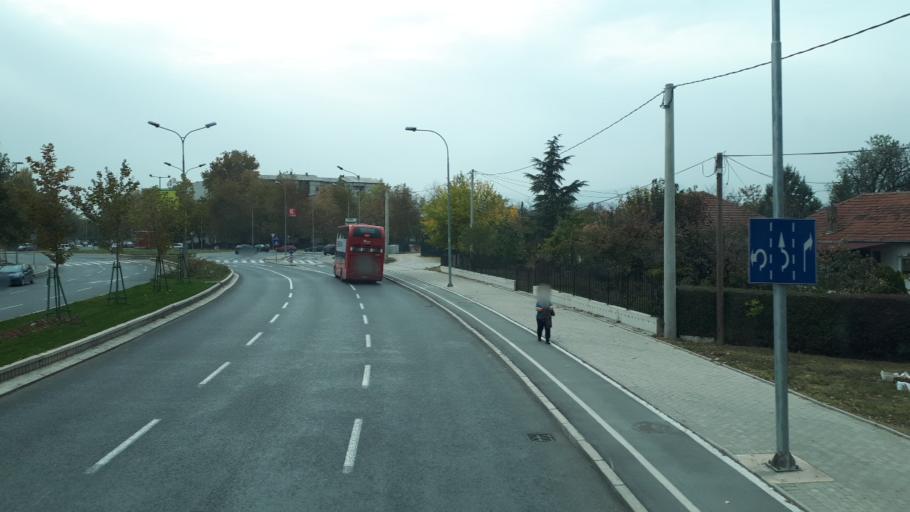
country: MK
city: Krushopek
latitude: 42.0102
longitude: 21.3629
